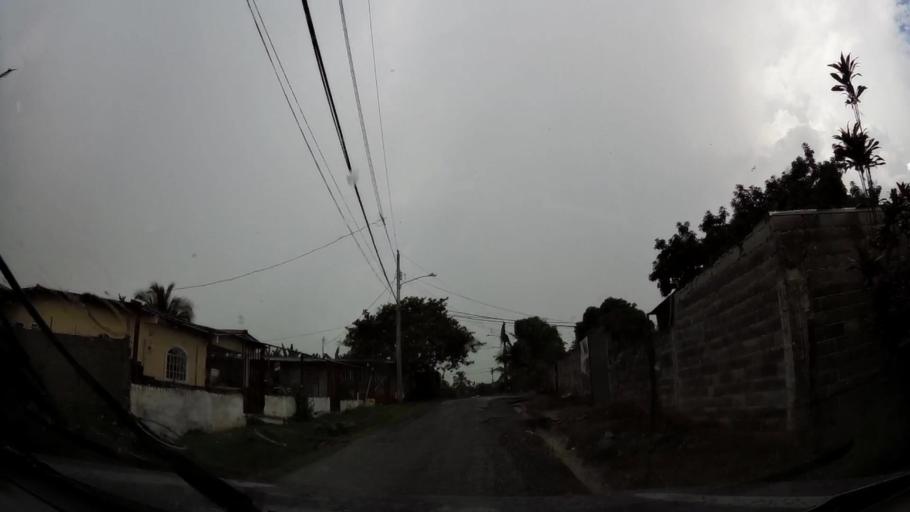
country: PA
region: Panama
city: Cabra Numero Uno
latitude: 9.1092
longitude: -79.3374
